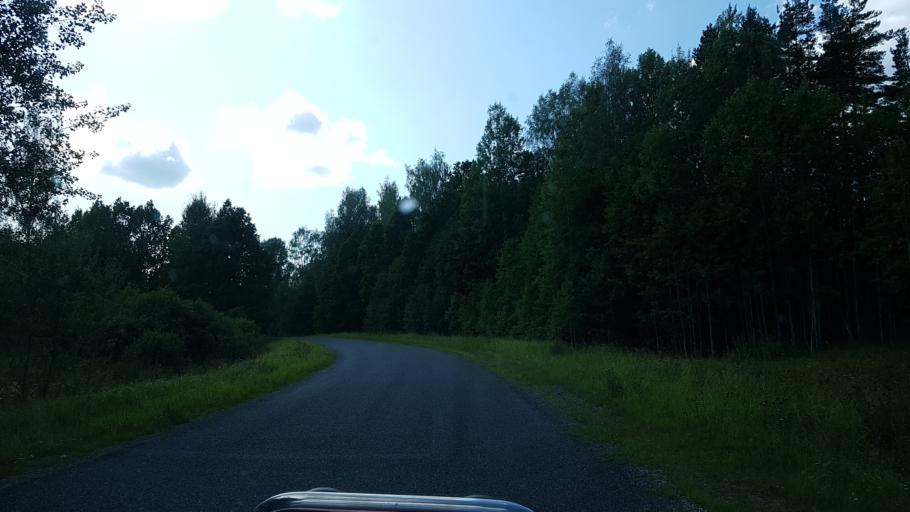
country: LV
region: Aluksnes Rajons
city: Aluksne
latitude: 57.6010
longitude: 27.0942
